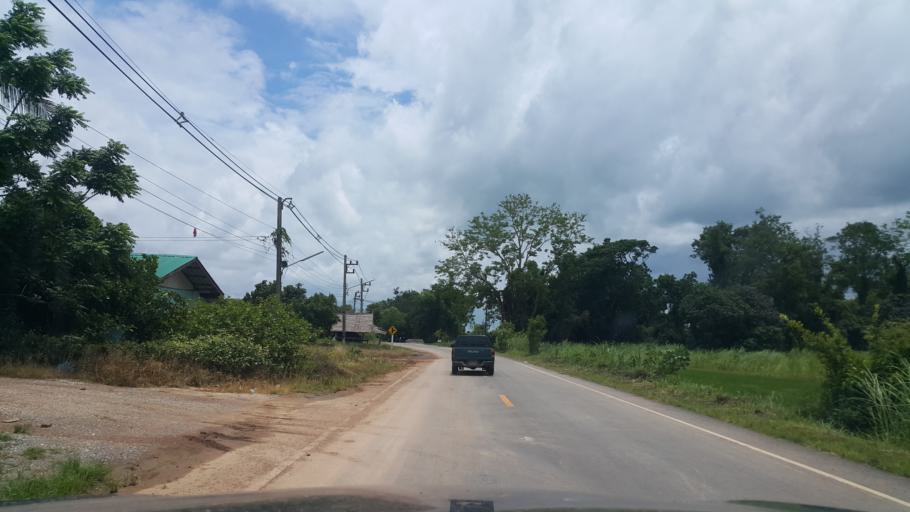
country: TH
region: Sukhothai
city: Kong Krailat
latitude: 16.9339
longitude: 99.9360
